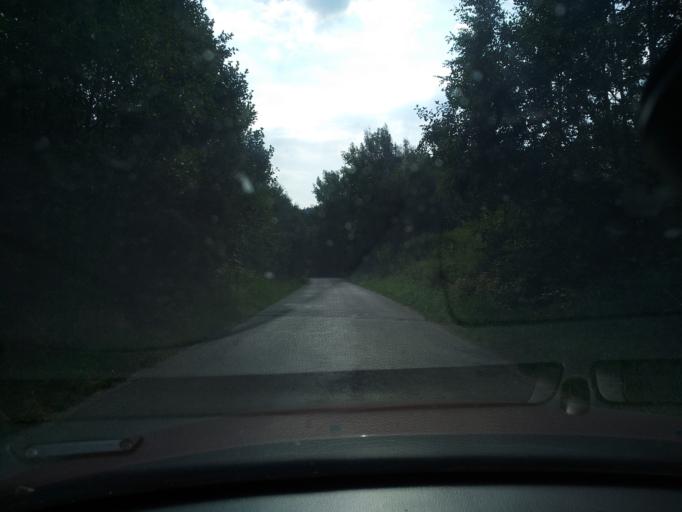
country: PL
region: Lower Silesian Voivodeship
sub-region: Powiat jeleniogorski
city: Stara Kamienica
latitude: 50.8816
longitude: 15.5535
